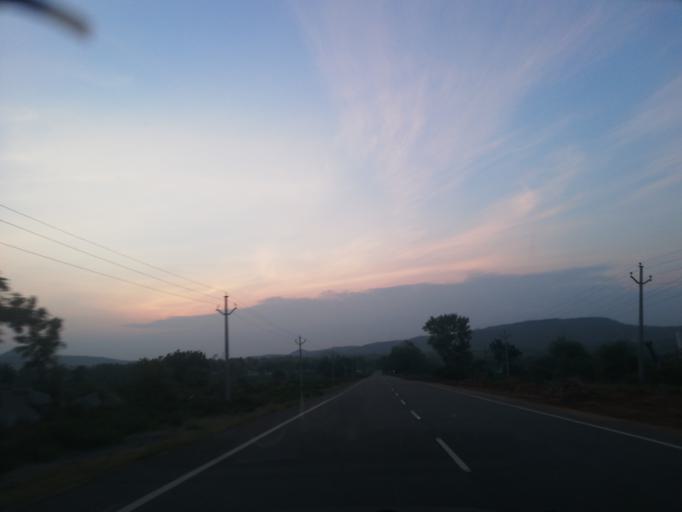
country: IN
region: Andhra Pradesh
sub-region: Guntur
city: Macherla
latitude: 16.6734
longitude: 79.2740
